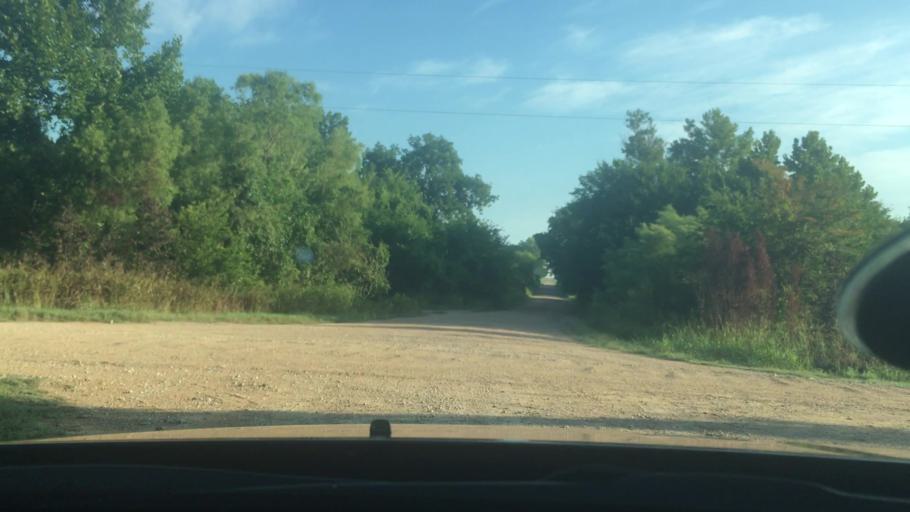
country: US
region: Oklahoma
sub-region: Pontotoc County
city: Ada
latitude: 34.8111
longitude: -96.7749
